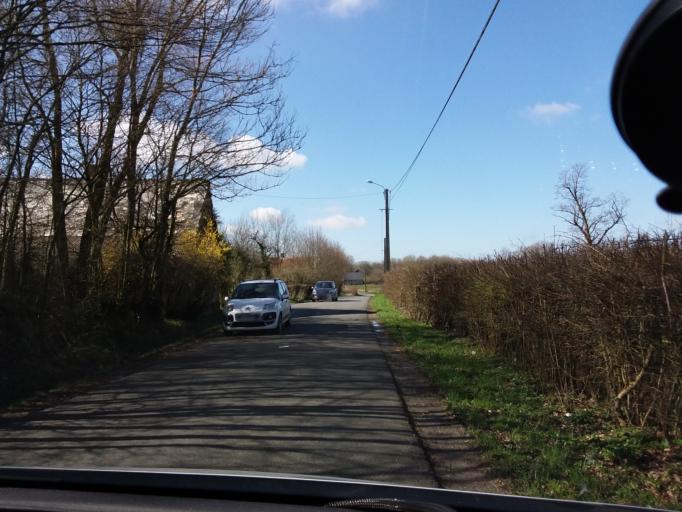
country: FR
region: Picardie
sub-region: Departement de l'Aisne
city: Origny-en-Thierache
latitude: 49.8393
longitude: 4.0647
